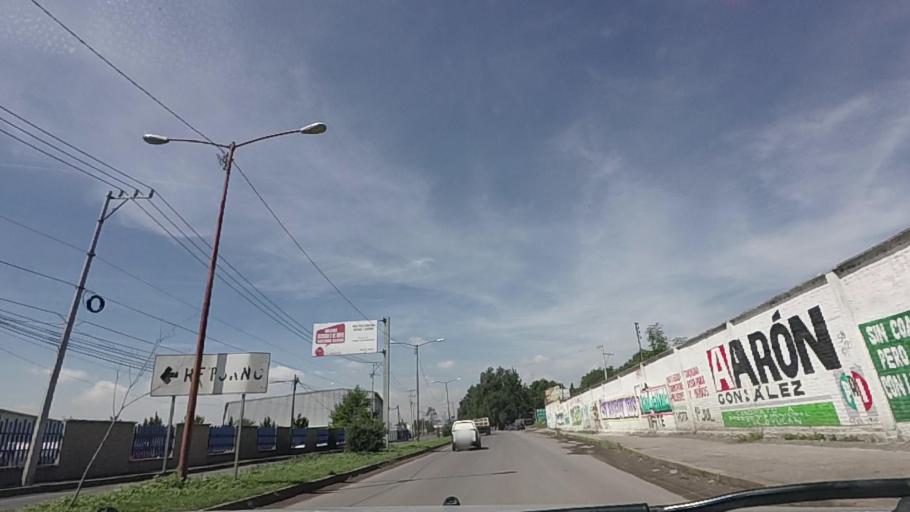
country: MX
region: Mexico
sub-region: Cuautitlan
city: San Jose del Puente
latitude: 19.7166
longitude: -99.1940
